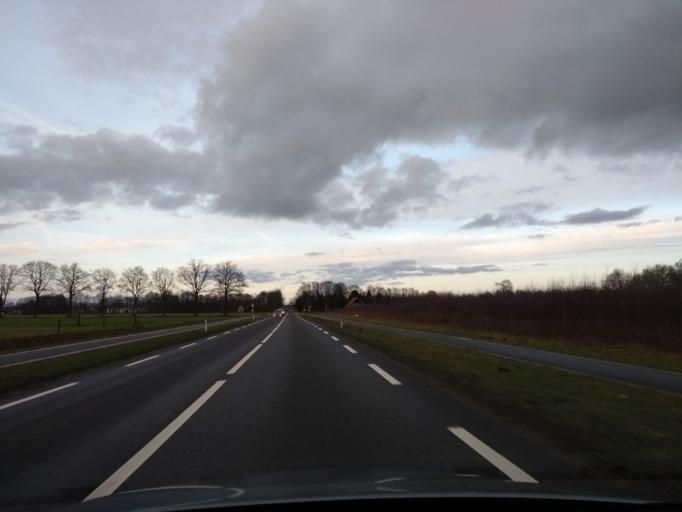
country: NL
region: Overijssel
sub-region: Gemeente Oldenzaal
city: Oldenzaal
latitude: 52.3343
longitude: 6.8598
